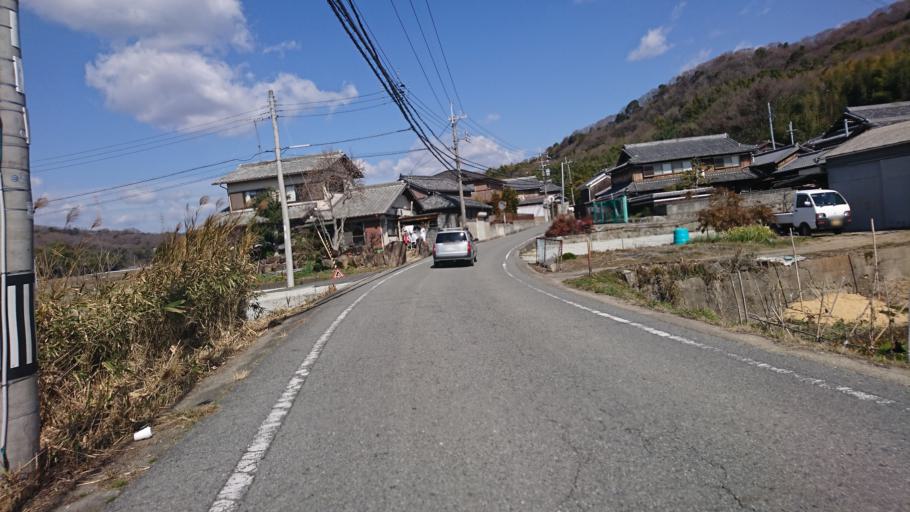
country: JP
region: Hyogo
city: Kakogawacho-honmachi
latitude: 34.8250
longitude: 134.8218
